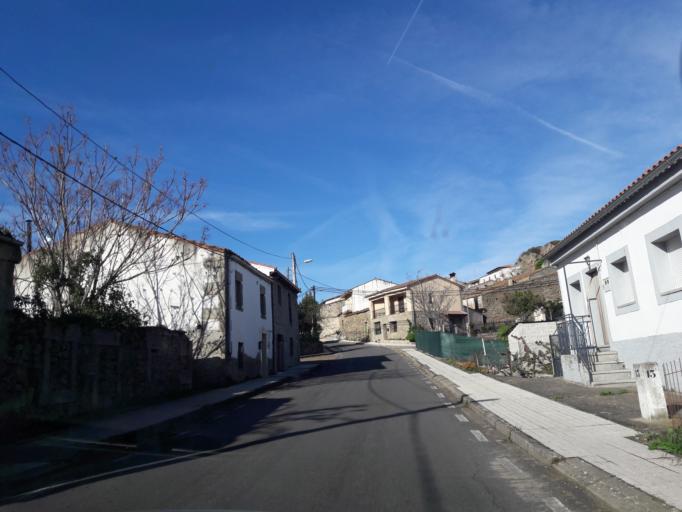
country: ES
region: Castille and Leon
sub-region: Provincia de Salamanca
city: Sanchotello
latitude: 40.4395
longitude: -5.7508
